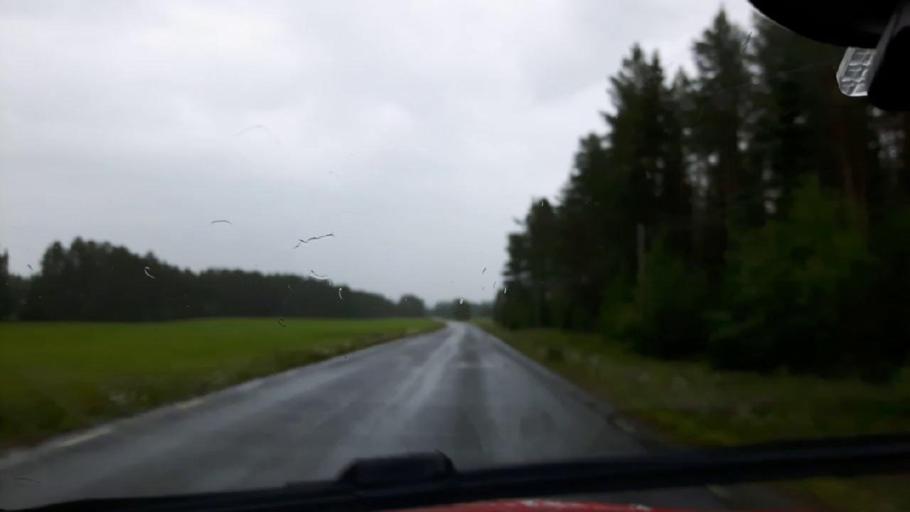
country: SE
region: Jaemtland
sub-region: OEstersunds Kommun
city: Brunflo
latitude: 62.9979
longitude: 14.7648
